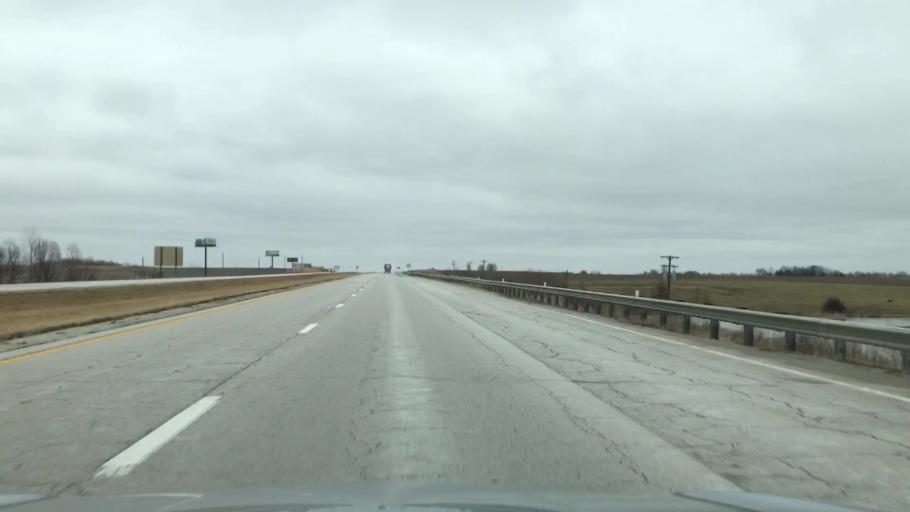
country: US
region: Missouri
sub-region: Caldwell County
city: Hamilton
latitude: 39.7334
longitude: -93.9978
